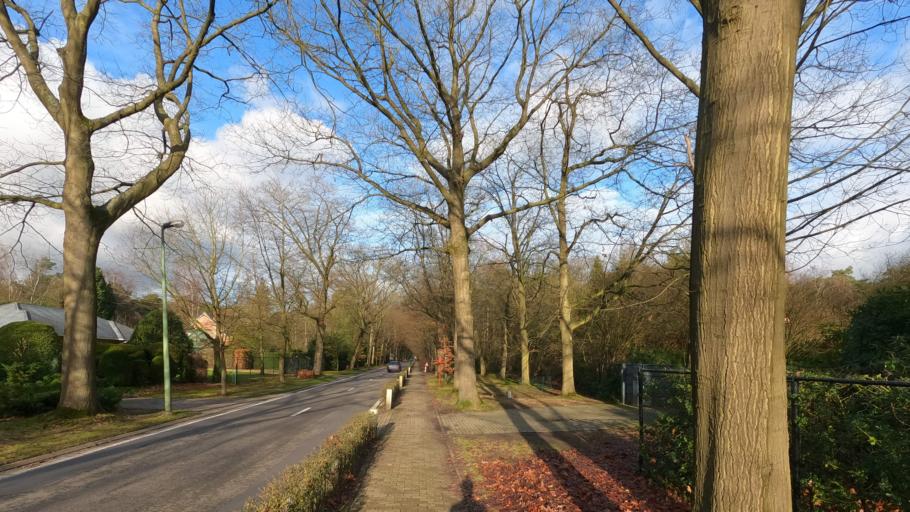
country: BE
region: Flanders
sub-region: Provincie Antwerpen
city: Schilde
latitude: 51.2733
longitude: 4.5697
